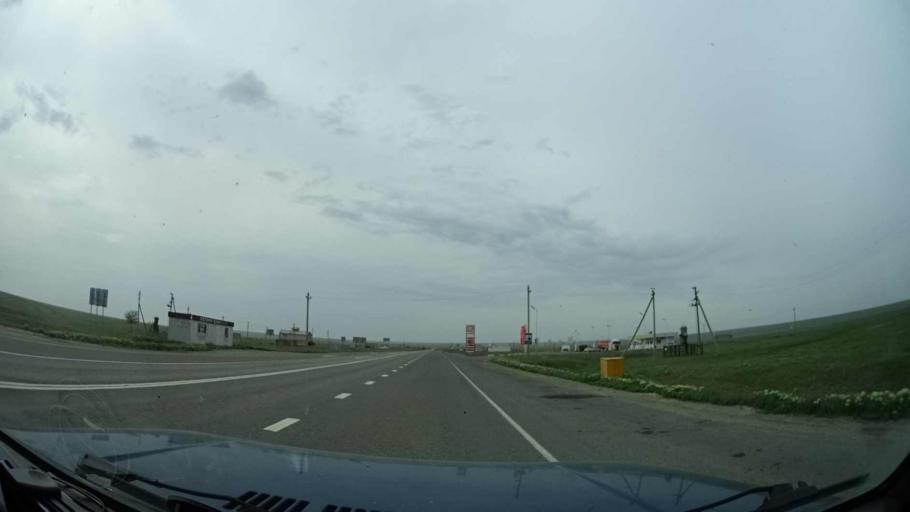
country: RU
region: Kalmykiya
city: Sovetskoye
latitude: 47.2983
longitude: 44.5726
